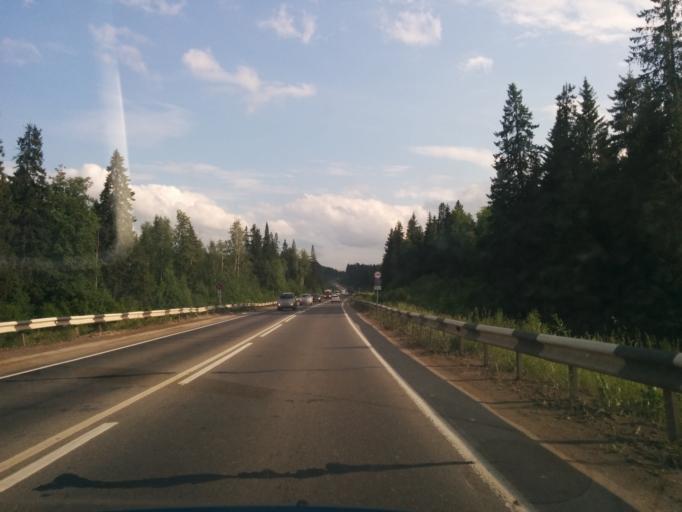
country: RU
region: Perm
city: Novyye Lyady
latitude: 58.0922
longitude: 56.4275
